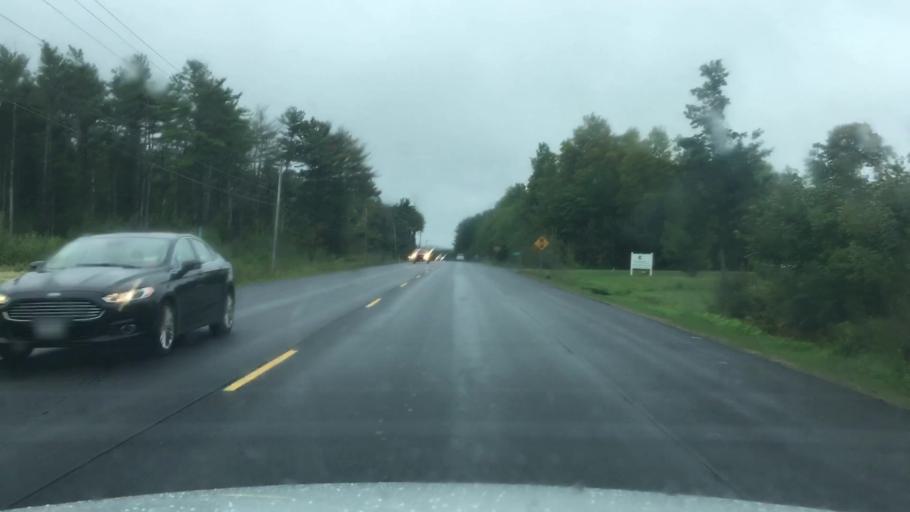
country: US
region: Maine
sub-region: Penobscot County
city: Hampden
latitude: 44.7577
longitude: -68.8441
